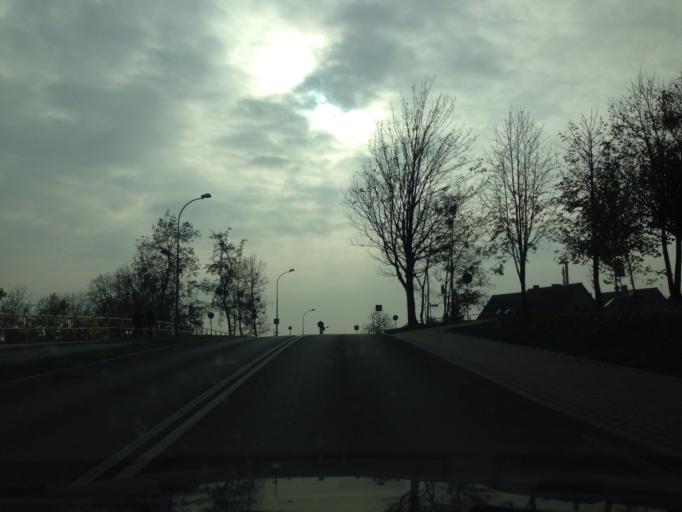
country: PL
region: Kujawsko-Pomorskie
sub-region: Powiat swiecki
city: Swiecie
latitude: 53.4122
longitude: 18.4428
